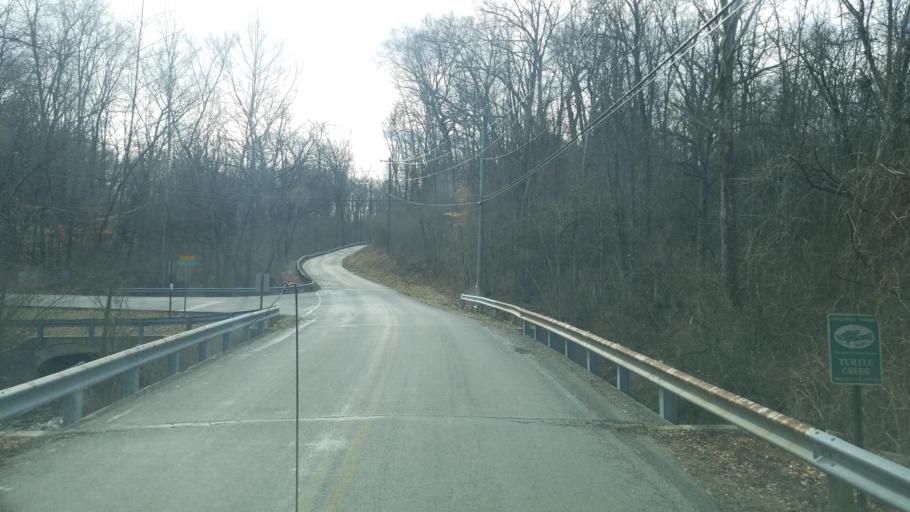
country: US
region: Ohio
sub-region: Warren County
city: Lebanon
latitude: 39.4263
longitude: -84.1599
